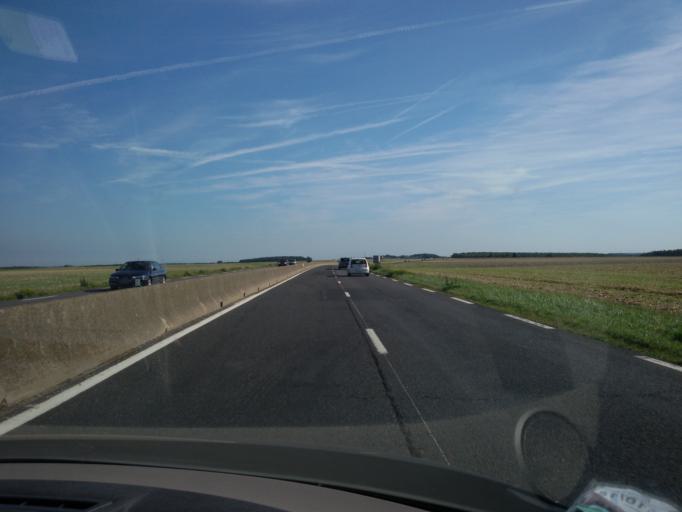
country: FR
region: Ile-de-France
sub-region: Departement de l'Essonne
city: Saclas
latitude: 48.3806
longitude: 2.0897
